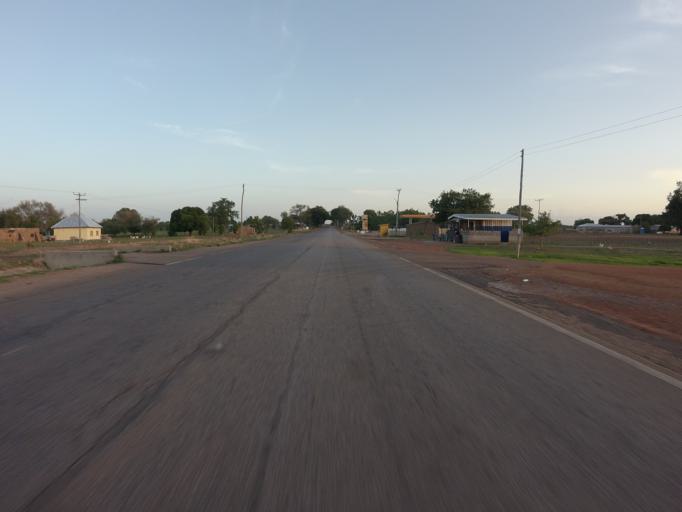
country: GH
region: Upper East
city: Navrongo
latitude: 10.9243
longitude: -1.0892
